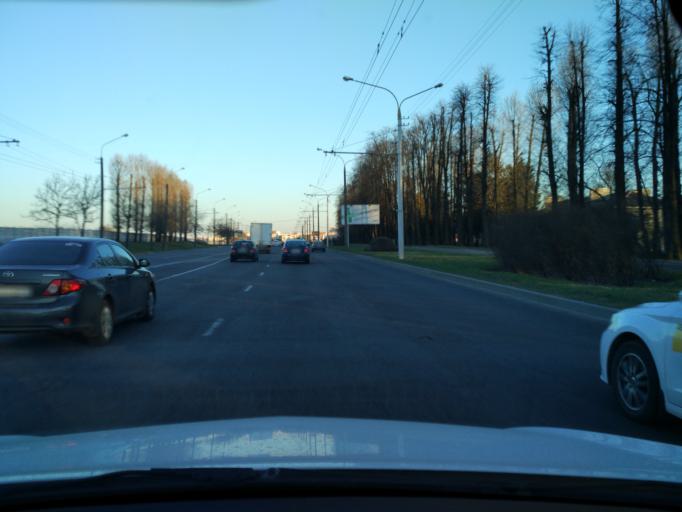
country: BY
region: Minsk
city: Syenitsa
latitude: 53.8644
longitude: 27.5310
